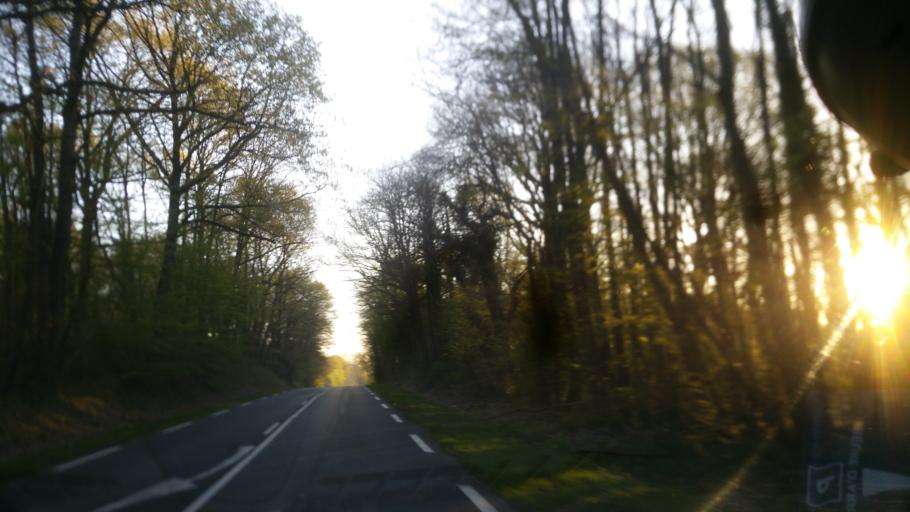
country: FR
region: Ile-de-France
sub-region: Departement de l'Essonne
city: Angervilliers
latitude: 48.5830
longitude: 2.0515
